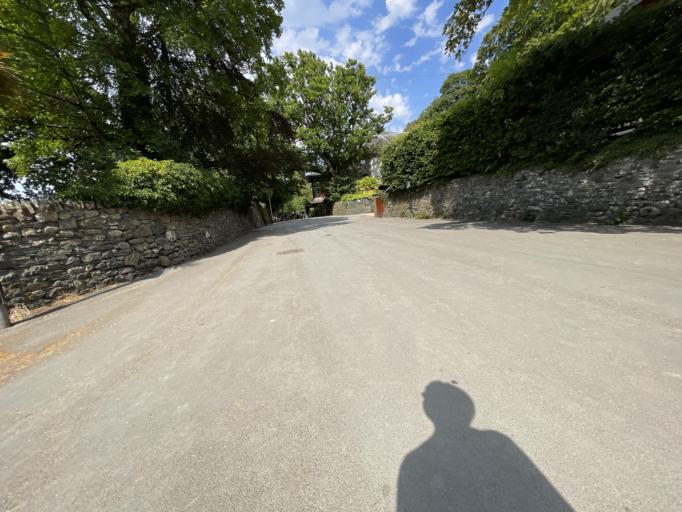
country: GB
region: England
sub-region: Cumbria
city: Keswick
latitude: 54.5952
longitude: -3.1400
